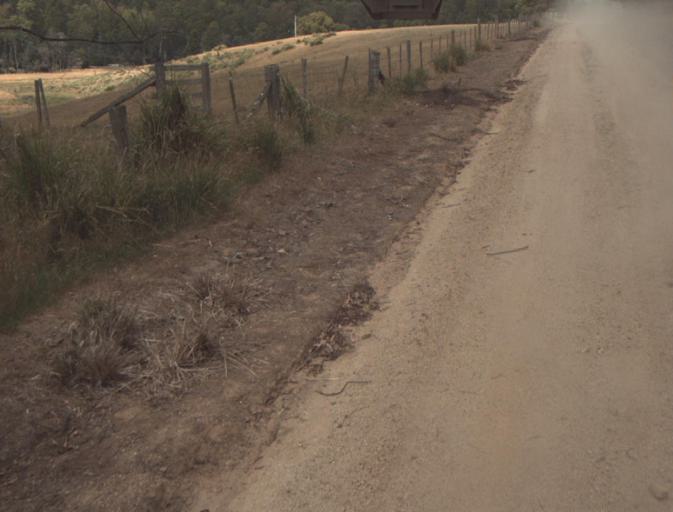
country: AU
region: Tasmania
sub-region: Dorset
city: Scottsdale
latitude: -41.4122
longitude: 147.5261
